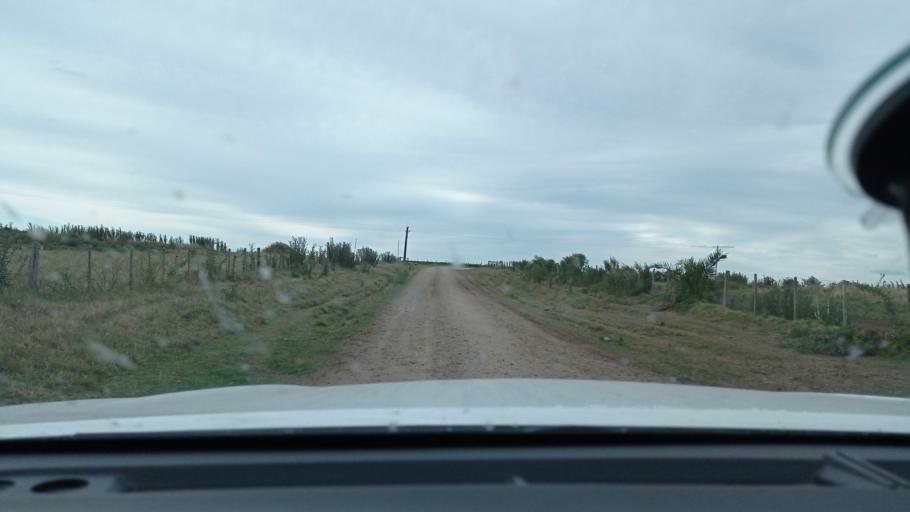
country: UY
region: Florida
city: Casupa
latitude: -34.1045
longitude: -55.7549
